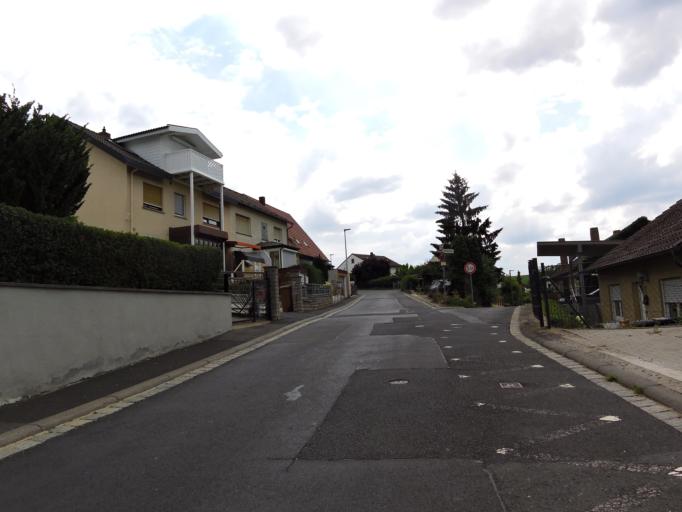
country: DE
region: Bavaria
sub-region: Regierungsbezirk Unterfranken
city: Eibelstadt
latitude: 49.7185
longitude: 9.9615
